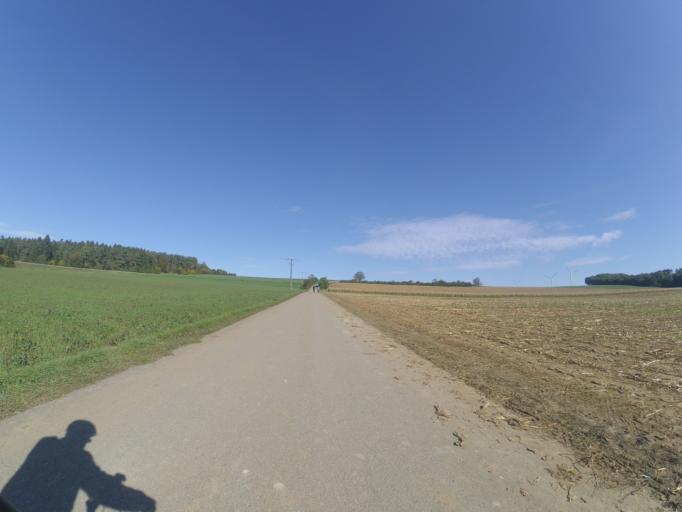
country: DE
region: Baden-Wuerttemberg
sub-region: Tuebingen Region
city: Breitingen
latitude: 48.5194
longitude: 9.9927
